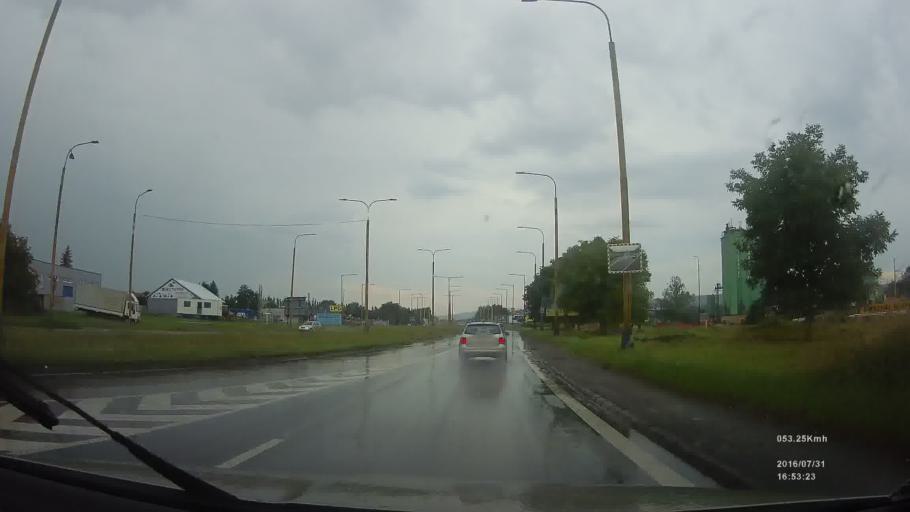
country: SK
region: Presovsky
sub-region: Okres Presov
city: Presov
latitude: 49.0139
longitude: 21.2671
